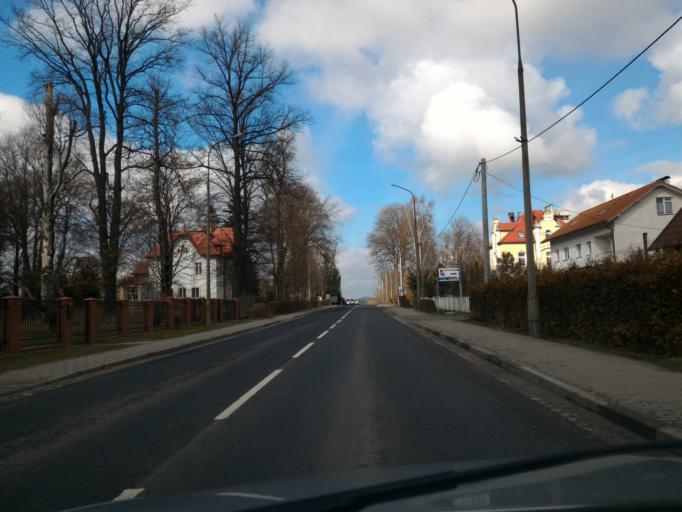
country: PL
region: Silesian Voivodeship
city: Zawidow
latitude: 51.0300
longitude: 15.0575
